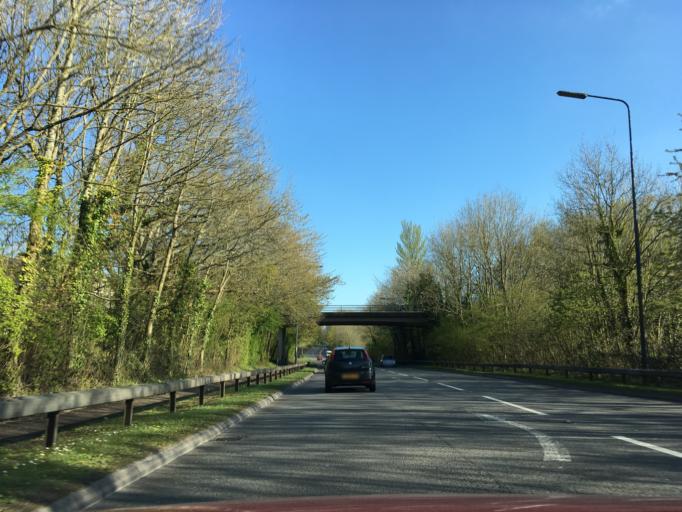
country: GB
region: Wales
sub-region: Torfaen County Borough
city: Cwmbran
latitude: 51.6258
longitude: -3.0152
